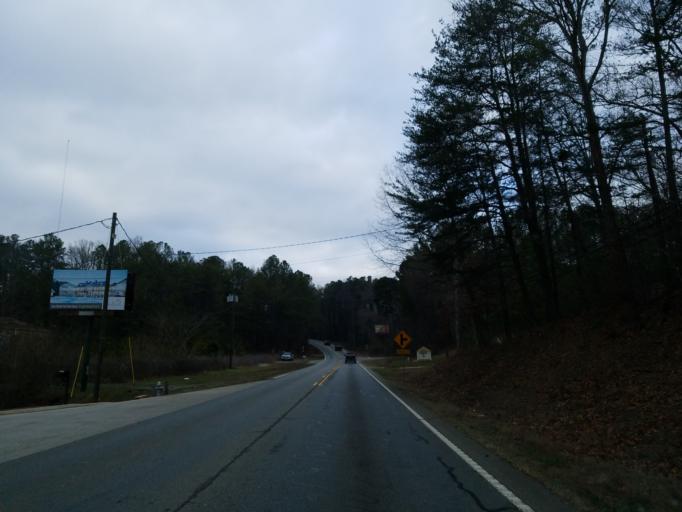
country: US
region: Georgia
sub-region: Cherokee County
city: Canton
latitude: 34.2662
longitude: -84.4947
